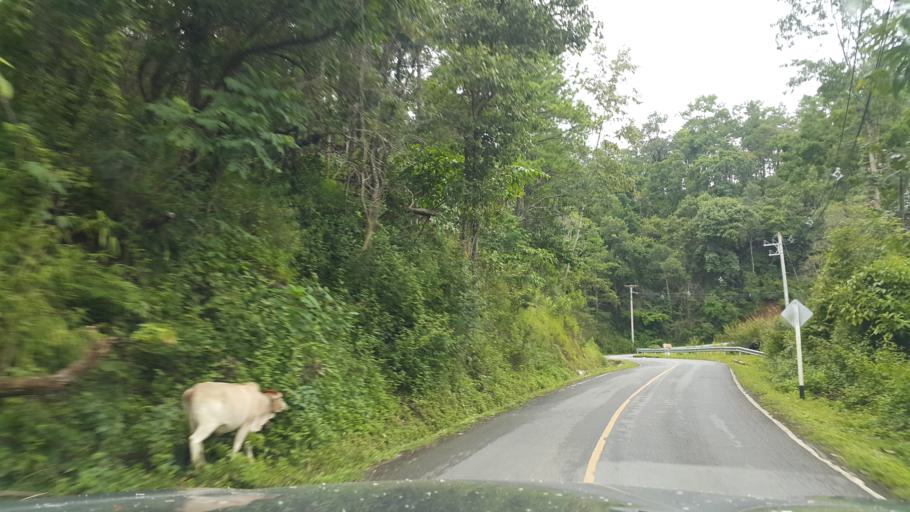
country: TH
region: Chiang Mai
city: Samoeng
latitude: 18.8832
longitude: 98.5347
